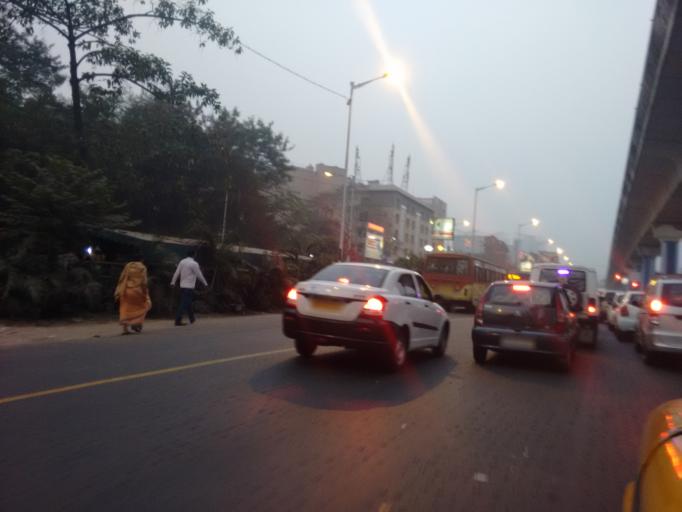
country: IN
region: West Bengal
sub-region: Kolkata
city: Kolkata
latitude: 22.5739
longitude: 88.4029
